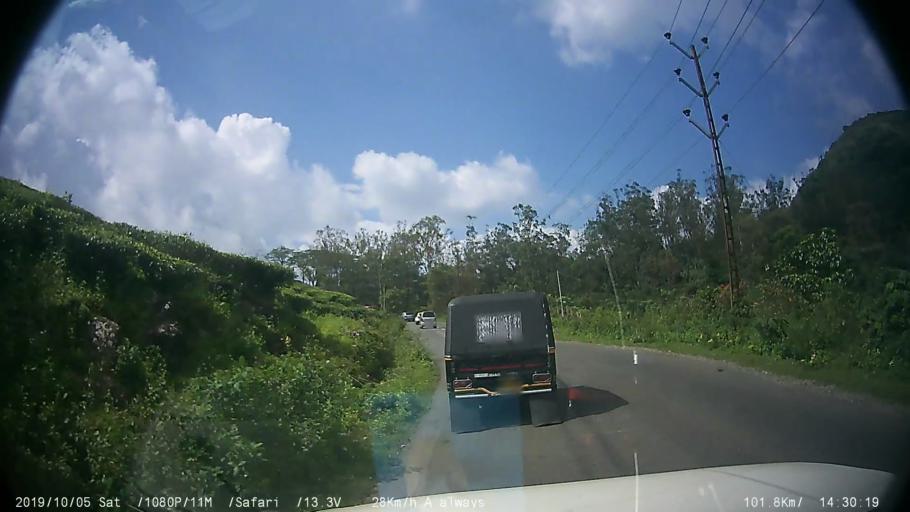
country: IN
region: Kerala
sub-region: Kottayam
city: Erattupetta
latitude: 9.6102
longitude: 76.9692
